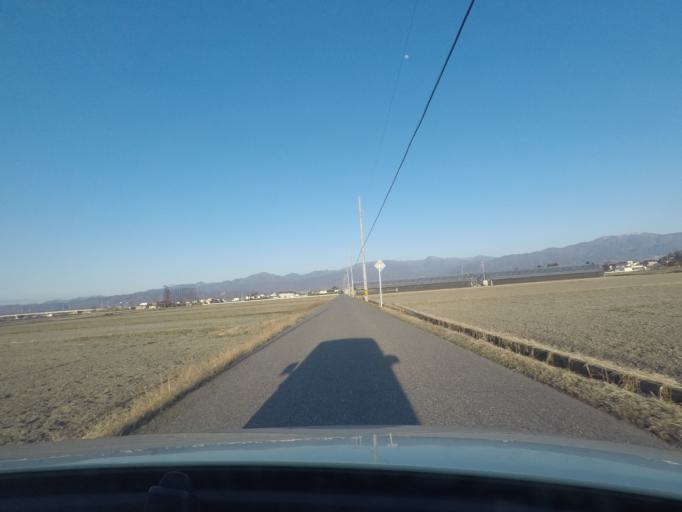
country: JP
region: Nagano
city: Matsumoto
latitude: 36.2197
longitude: 137.8948
